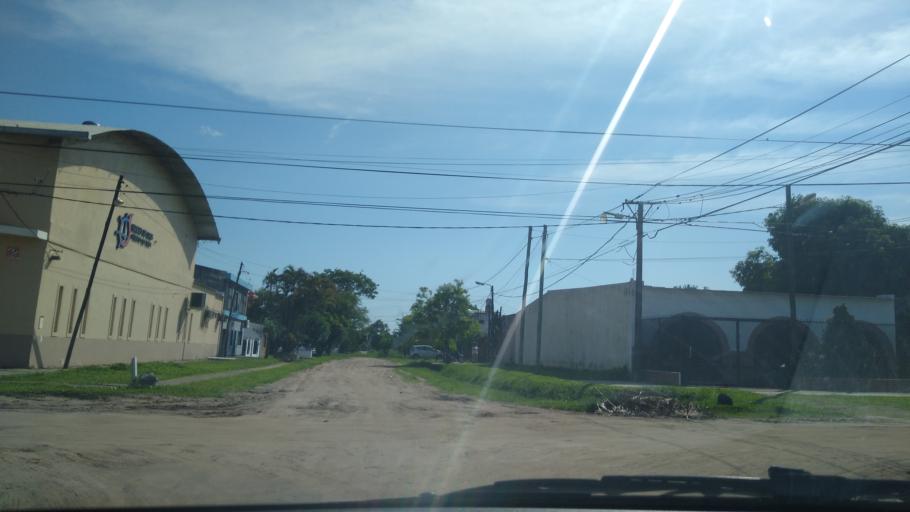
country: AR
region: Chaco
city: Barranqueras
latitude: -27.4870
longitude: -58.9529
